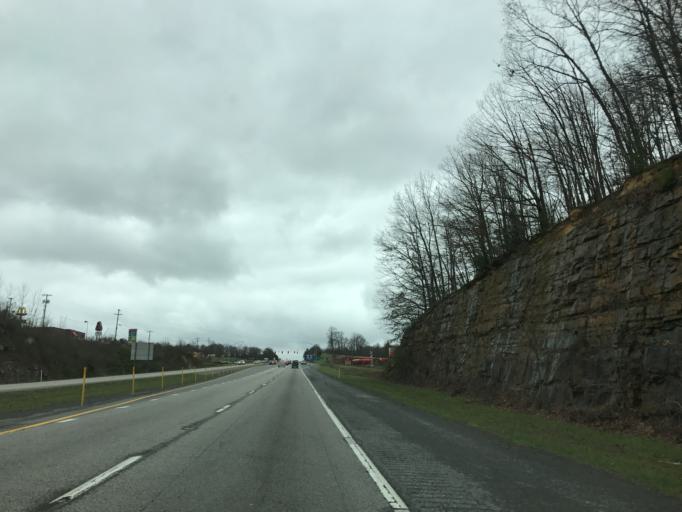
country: US
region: West Virginia
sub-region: Fayette County
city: Fayetteville
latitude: 38.0348
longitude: -81.1231
